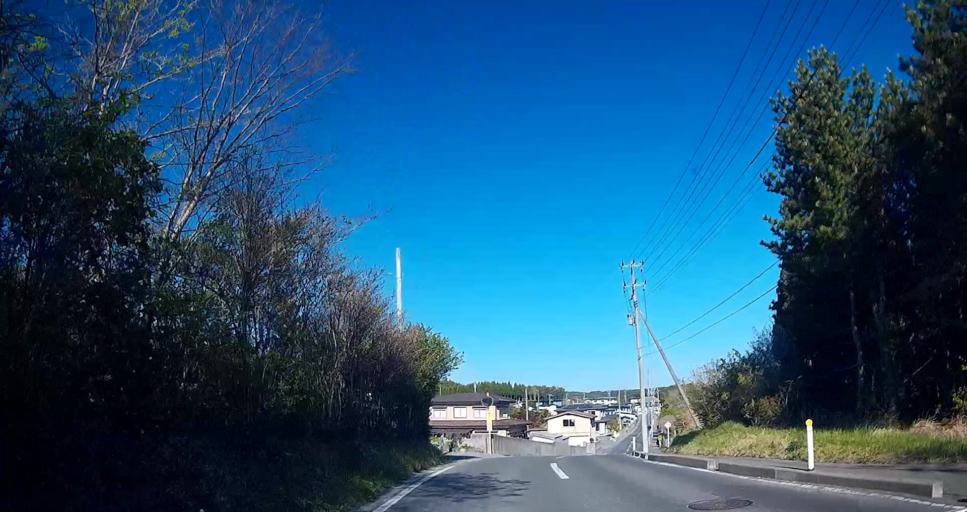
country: JP
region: Aomori
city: Hachinohe
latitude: 40.5146
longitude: 141.6021
